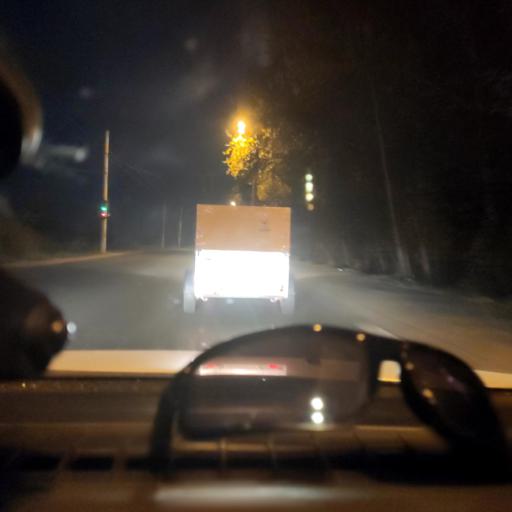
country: RU
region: Samara
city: Samara
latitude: 53.1556
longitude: 50.0917
